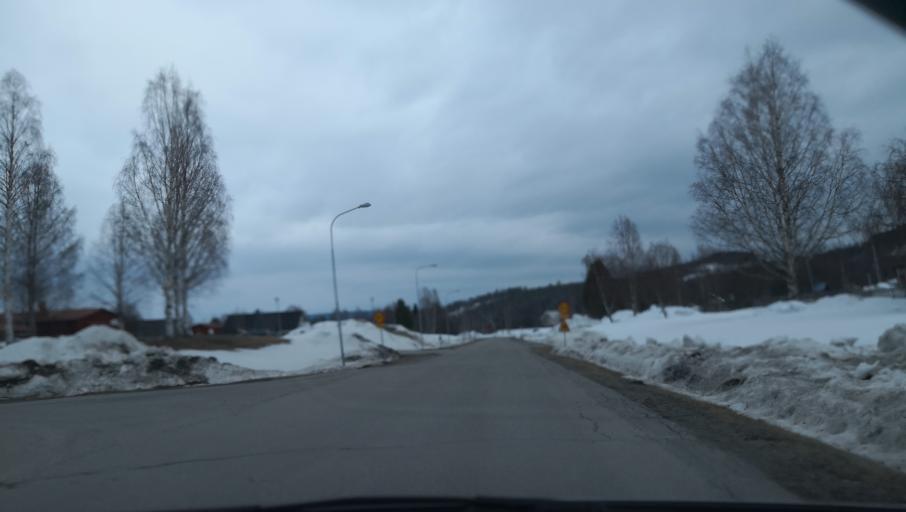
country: SE
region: Vaesterbotten
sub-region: Vannas Kommun
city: Vannasby
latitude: 63.9185
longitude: 19.8090
